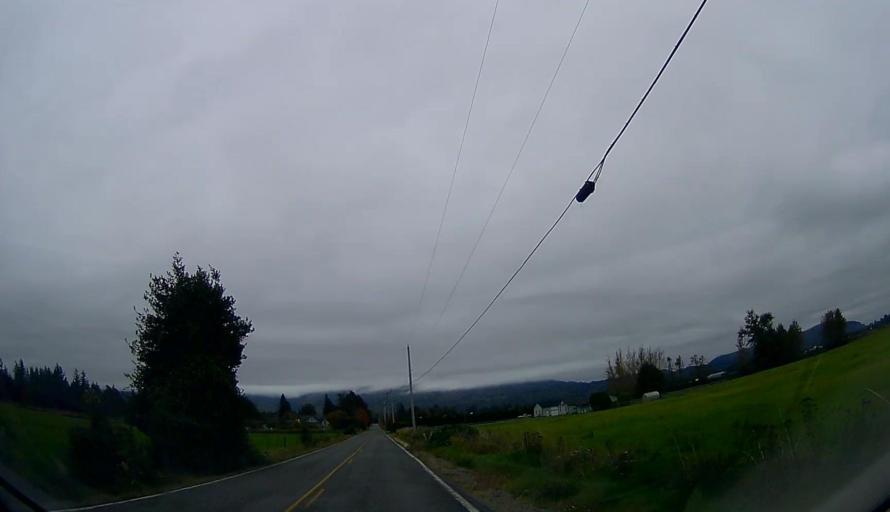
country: US
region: Washington
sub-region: Skagit County
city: Sedro-Woolley
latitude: 48.5244
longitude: -122.1400
